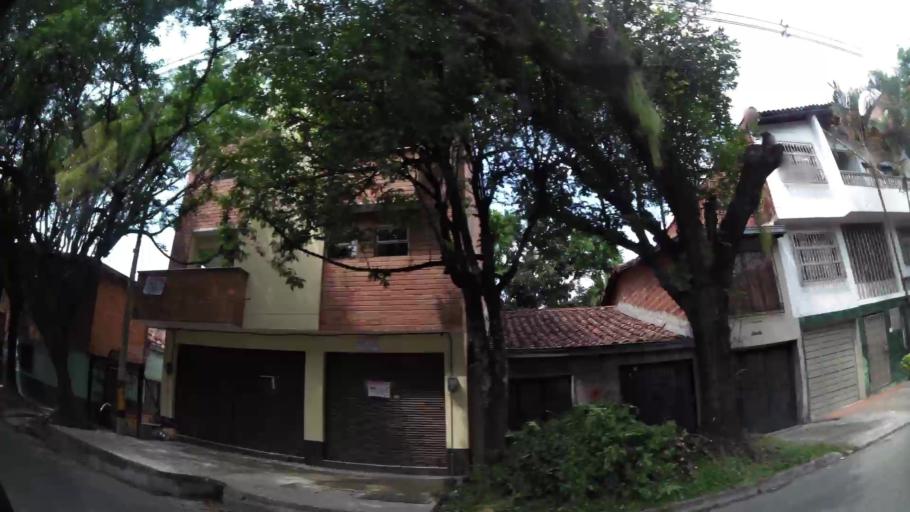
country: CO
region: Antioquia
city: Envigado
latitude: 6.1685
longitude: -75.5924
